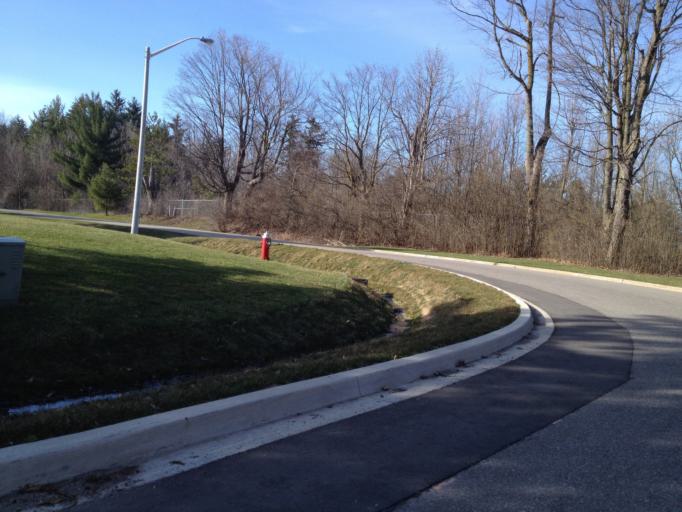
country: CA
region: Ontario
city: Brampton
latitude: 43.7403
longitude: -79.7986
